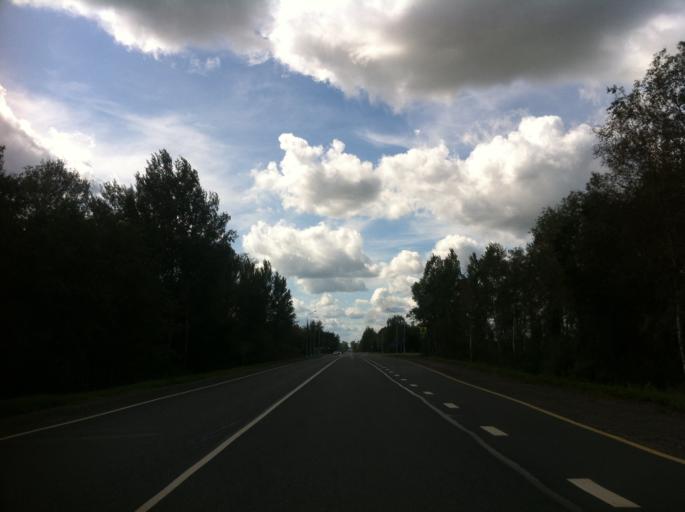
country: RU
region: Pskov
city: Pskov
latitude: 57.7674
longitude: 28.1148
